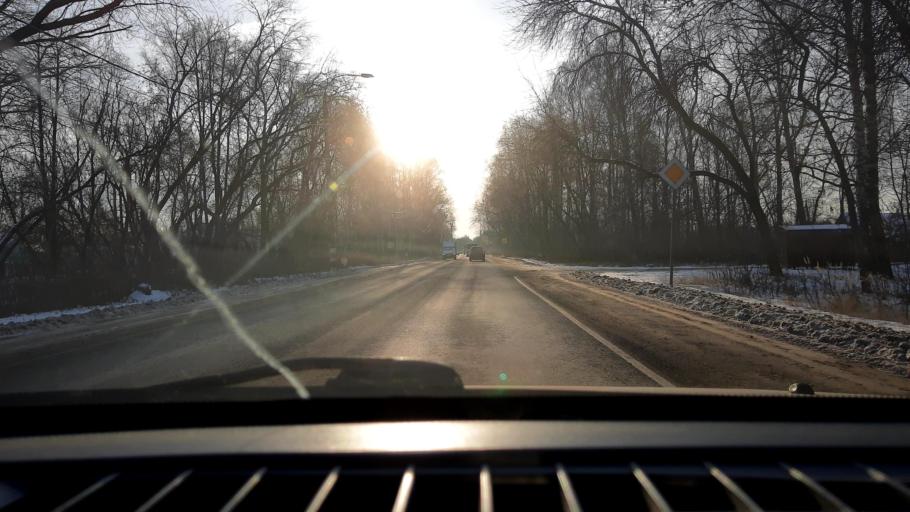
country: RU
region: Nizjnij Novgorod
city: Bor
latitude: 56.3644
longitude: 44.0869
